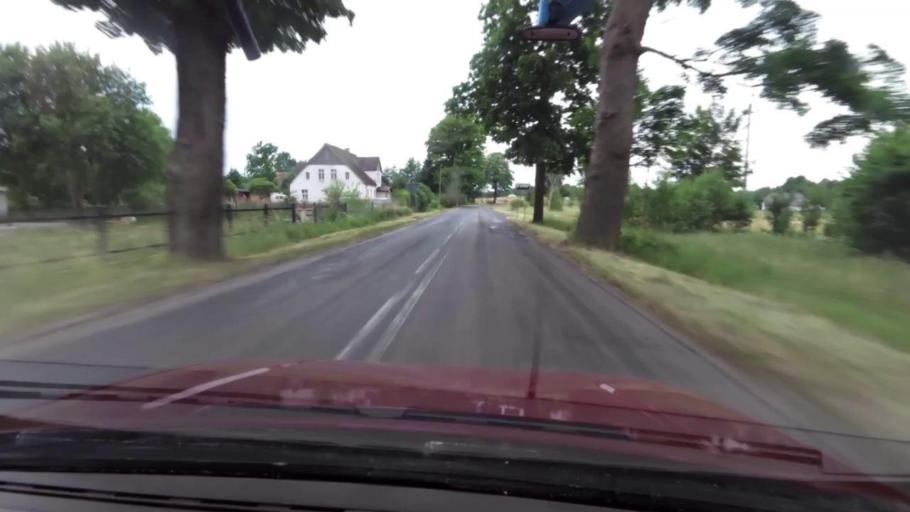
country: PL
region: West Pomeranian Voivodeship
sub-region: Powiat koszalinski
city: Sianow
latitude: 54.1771
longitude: 16.3862
